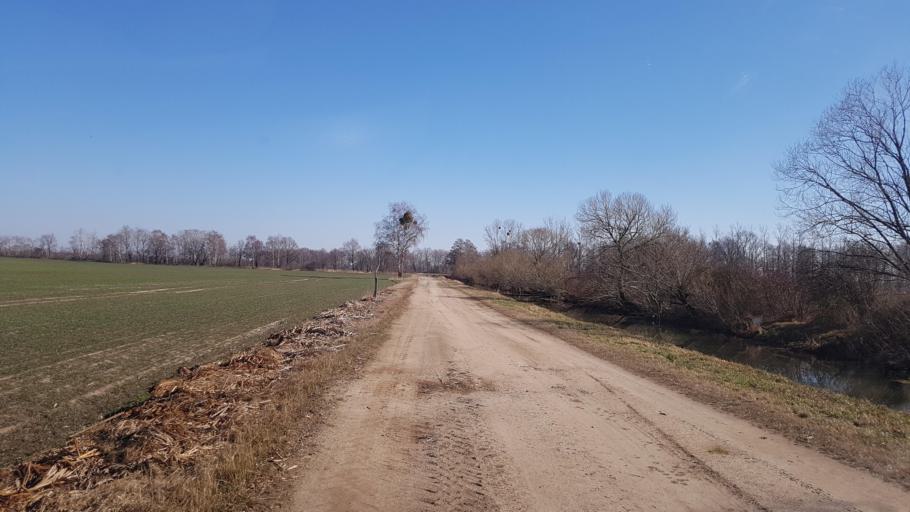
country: DE
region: Brandenburg
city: Grossthiemig
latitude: 51.4117
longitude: 13.6646
